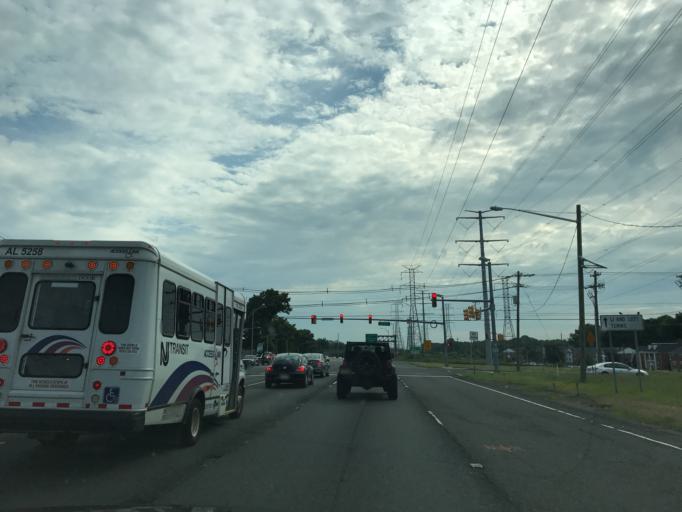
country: US
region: New Jersey
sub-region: Middlesex County
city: Fords
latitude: 40.5497
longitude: -74.3224
